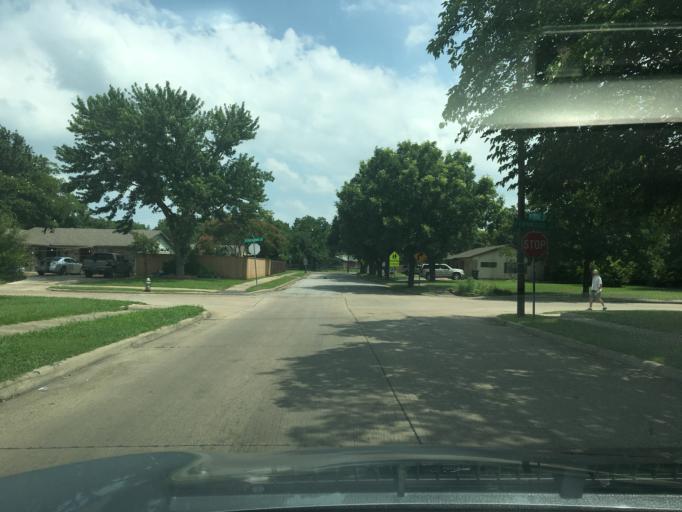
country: US
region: Texas
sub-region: Dallas County
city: Richardson
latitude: 32.9142
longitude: -96.6955
